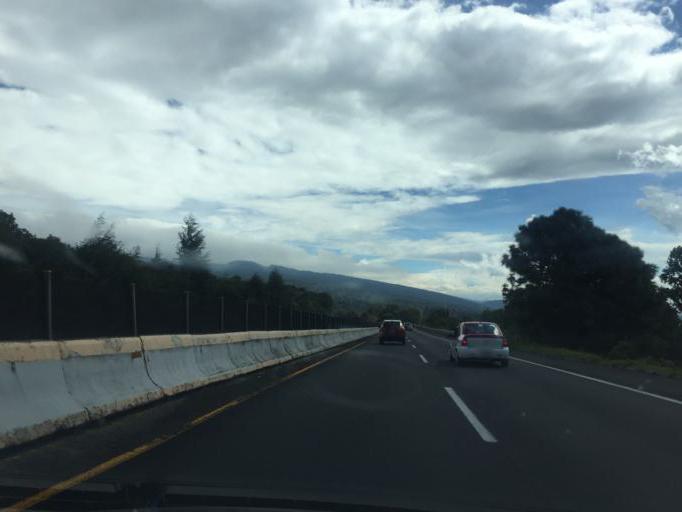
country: MX
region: Morelos
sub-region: Cuernavaca
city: Villa Santiago
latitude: 19.0245
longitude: -99.1915
